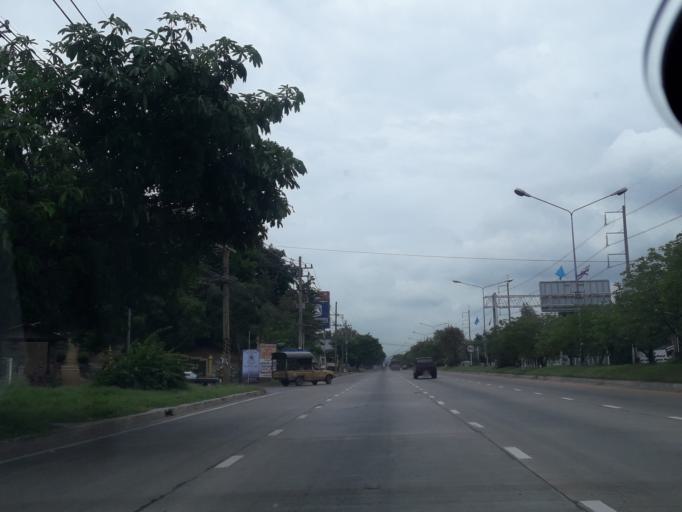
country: TH
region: Sara Buri
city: Phra Phutthabat
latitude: 14.7214
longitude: 100.8058
